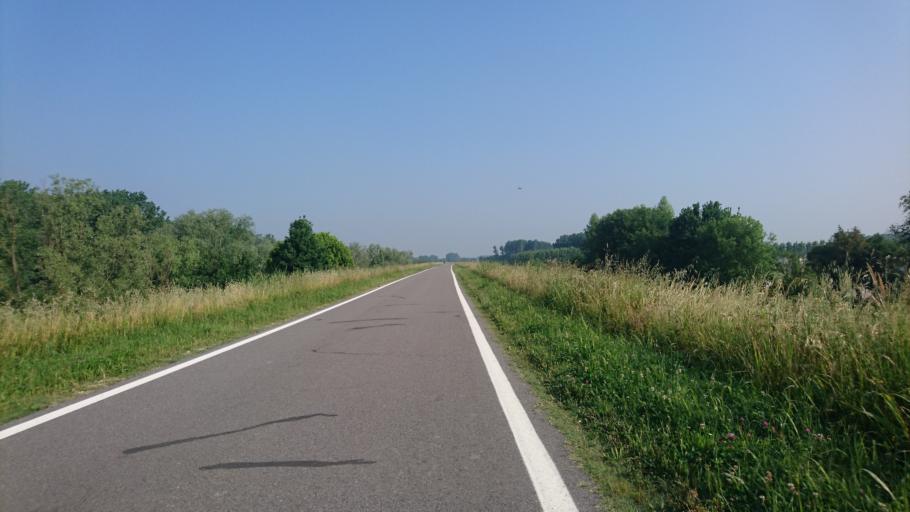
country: IT
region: Veneto
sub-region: Provincia di Rovigo
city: Castelnovo Bariano
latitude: 45.0255
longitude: 11.2726
